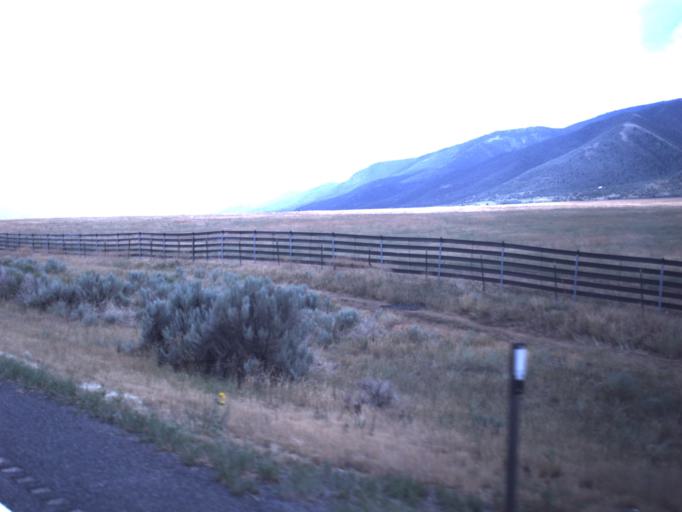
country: US
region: Utah
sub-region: Sanpete County
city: Fountain Green
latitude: 39.6732
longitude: -111.6653
